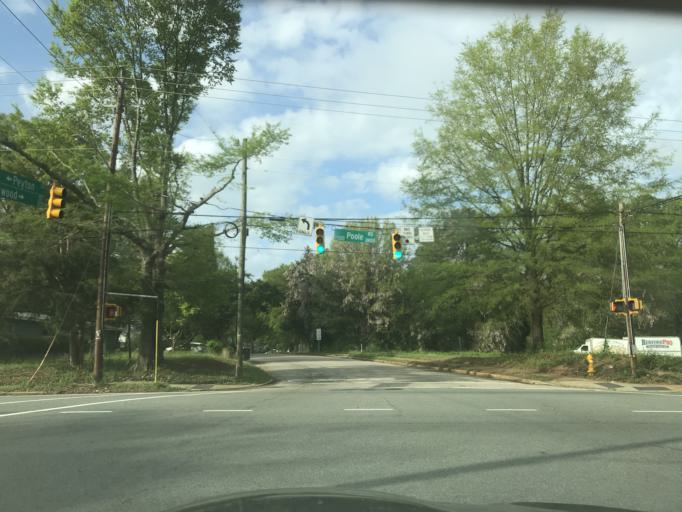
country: US
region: North Carolina
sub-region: Wake County
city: Raleigh
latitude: 35.7747
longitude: -78.6061
